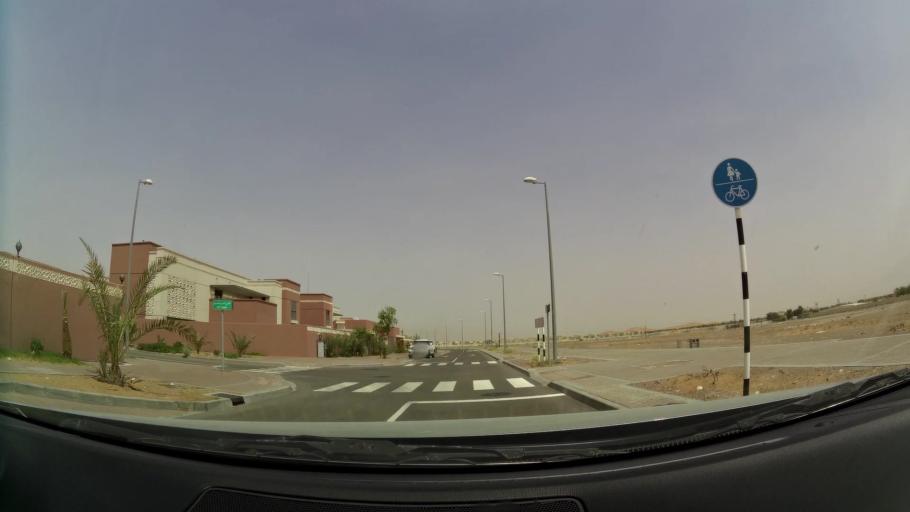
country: AE
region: Abu Dhabi
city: Al Ain
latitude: 24.1423
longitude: 55.6174
